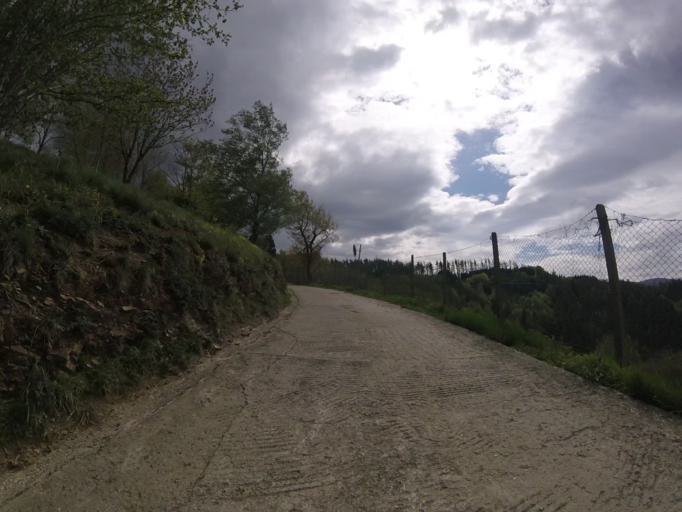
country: ES
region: Basque Country
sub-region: Provincia de Guipuzcoa
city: Aizarnazabal
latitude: 43.2465
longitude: -2.1937
